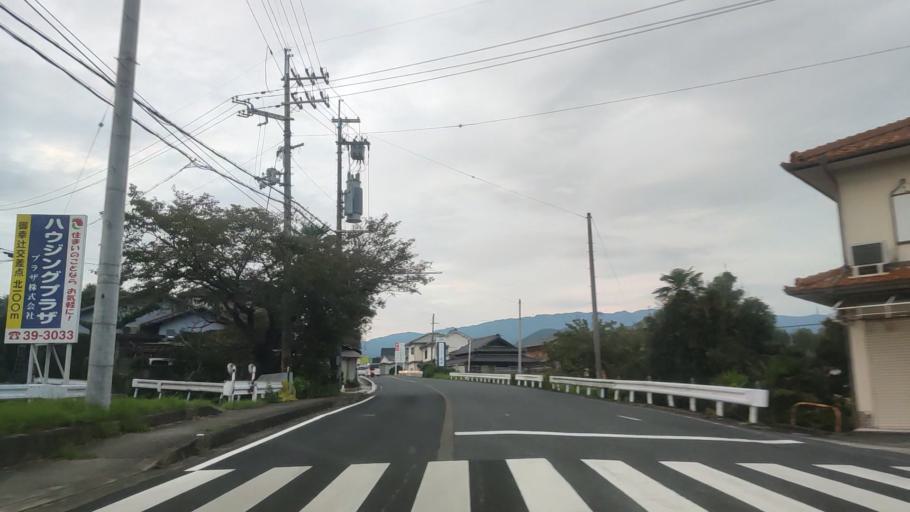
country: JP
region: Wakayama
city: Hashimoto
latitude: 34.3344
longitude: 135.6058
